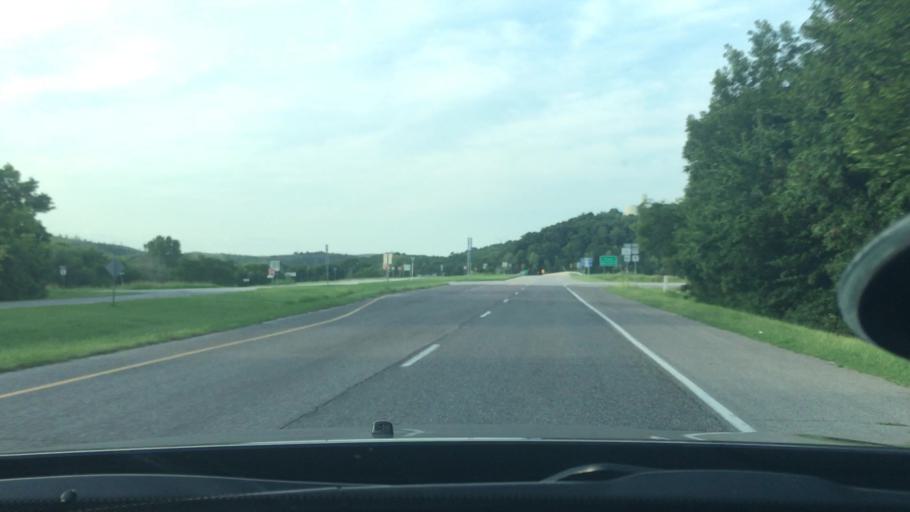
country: US
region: Oklahoma
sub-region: Murray County
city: Davis
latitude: 34.4538
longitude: -97.1341
